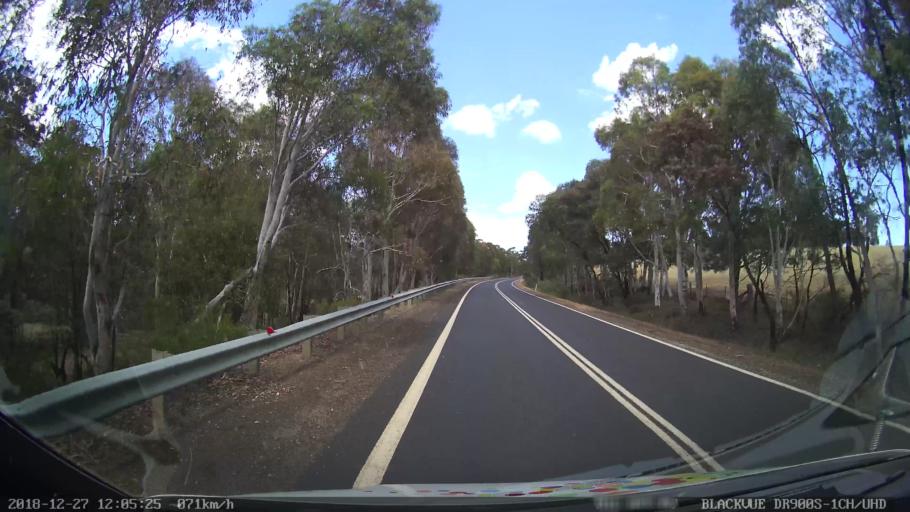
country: AU
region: New South Wales
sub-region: Blayney
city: Blayney
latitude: -33.8022
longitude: 149.3391
